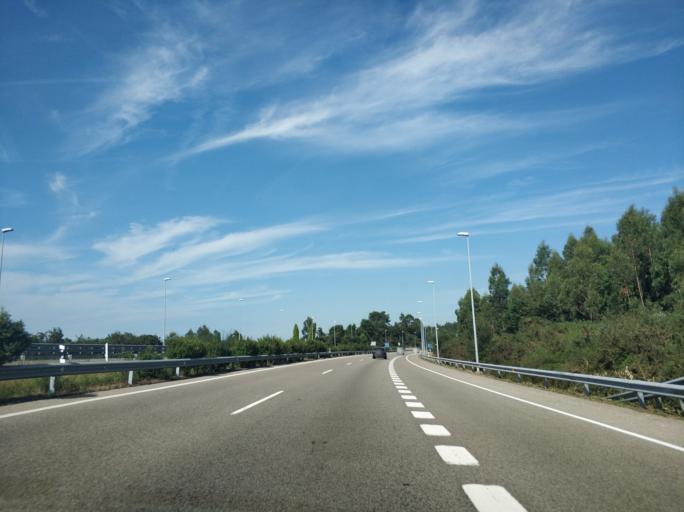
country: ES
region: Asturias
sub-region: Province of Asturias
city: Castrillon
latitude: 43.5483
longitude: -5.9992
